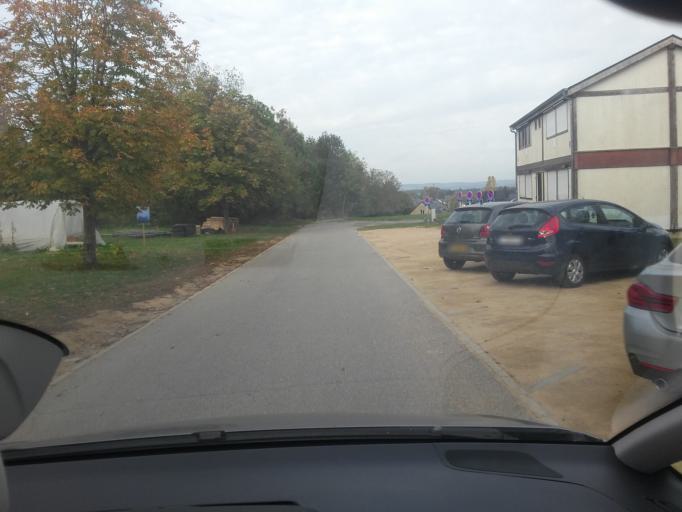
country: BE
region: Wallonia
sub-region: Province du Luxembourg
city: Arlon
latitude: 49.6913
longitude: 5.8227
